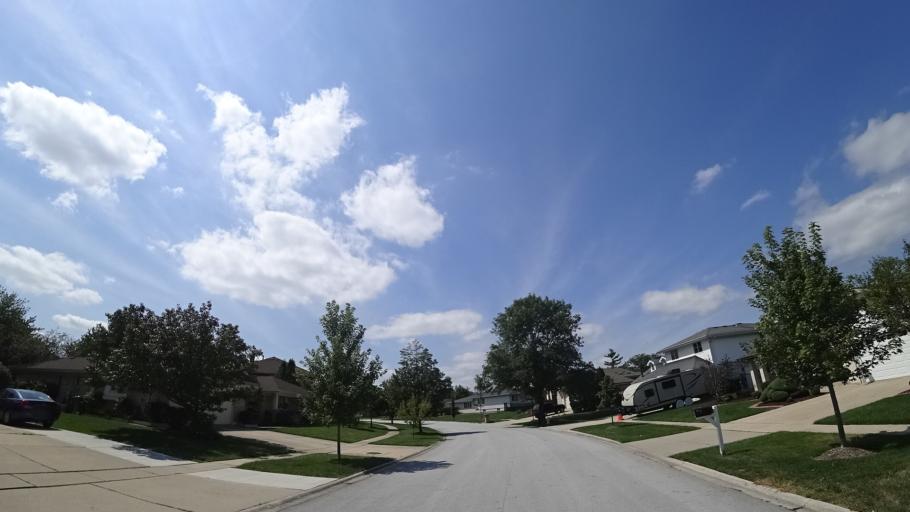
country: US
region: Illinois
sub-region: Cook County
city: Orland Hills
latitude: 41.5674
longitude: -87.8432
